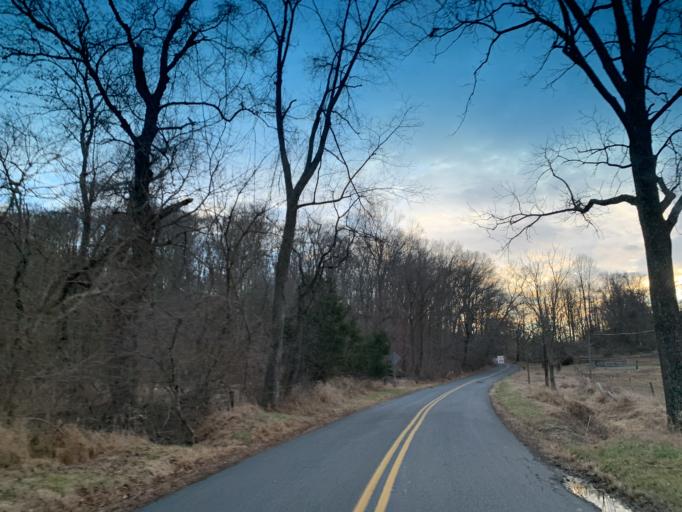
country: US
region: Maryland
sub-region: Harford County
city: South Bel Air
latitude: 39.6230
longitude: -76.3082
